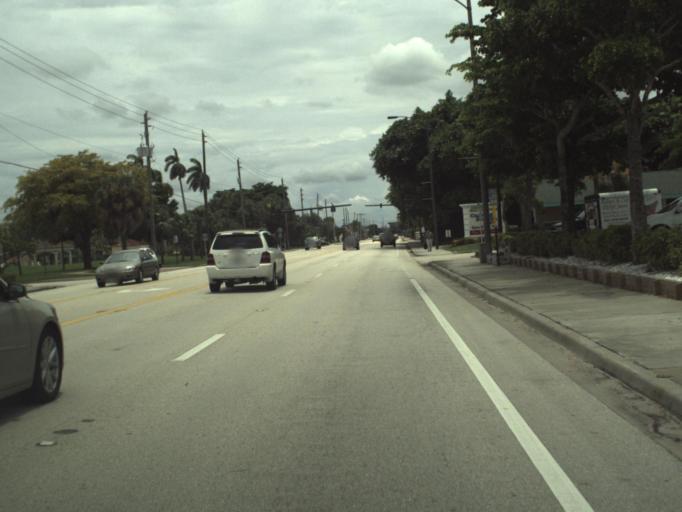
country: US
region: Florida
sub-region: Palm Beach County
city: Lake Park
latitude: 26.7997
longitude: -80.0549
